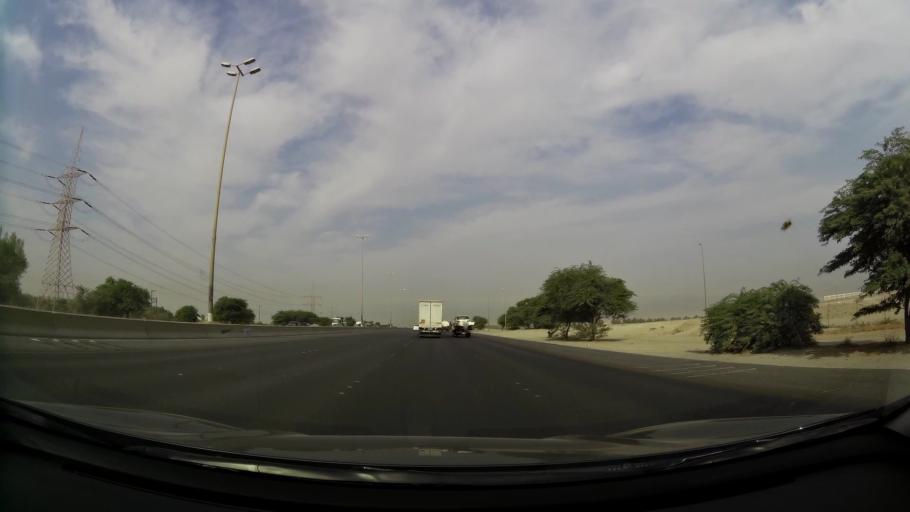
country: KW
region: Al Asimah
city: Ar Rabiyah
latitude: 29.2749
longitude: 47.8096
